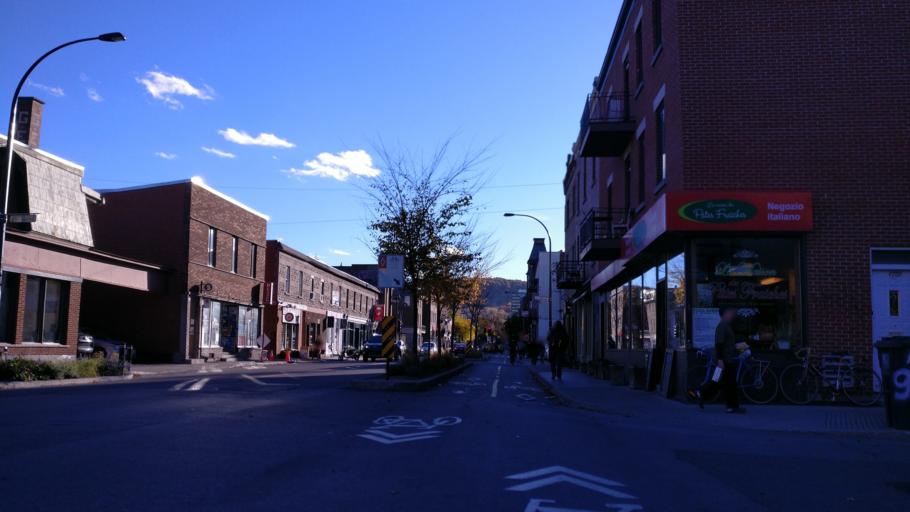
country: CA
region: Quebec
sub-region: Montreal
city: Montreal
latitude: 45.5243
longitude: -73.5759
